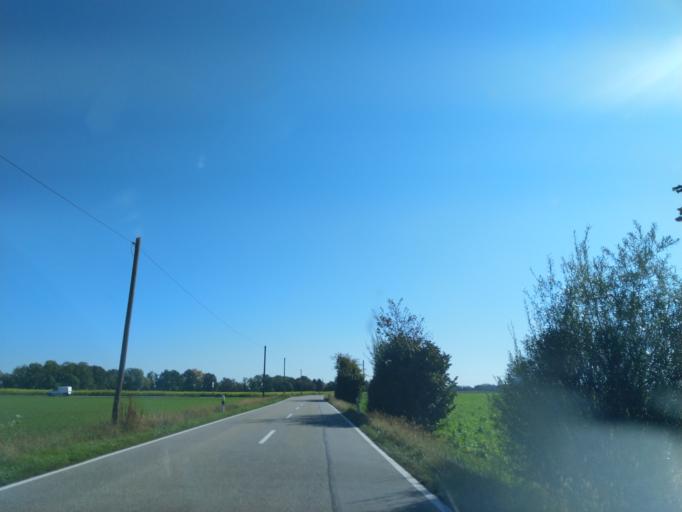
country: DE
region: Bavaria
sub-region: Lower Bavaria
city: Irlbach
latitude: 48.8386
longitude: 12.7600
